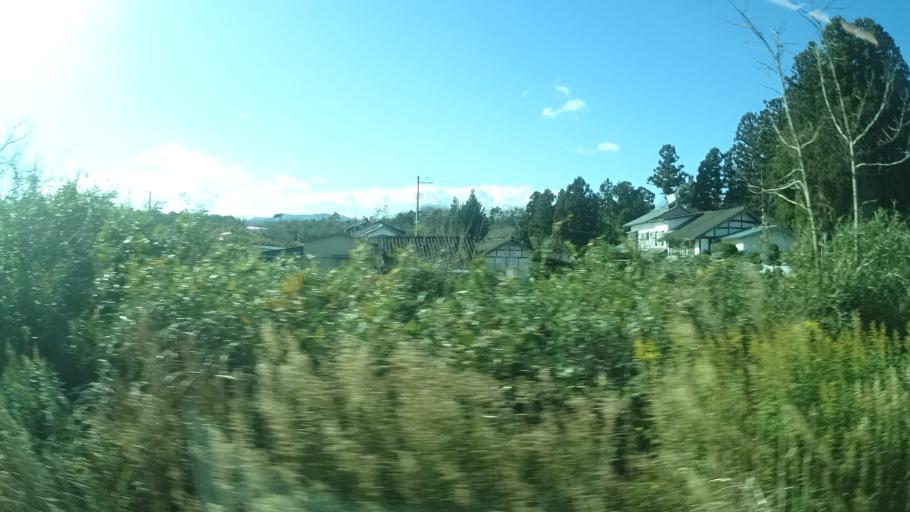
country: JP
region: Miyagi
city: Marumori
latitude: 37.7479
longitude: 140.9405
